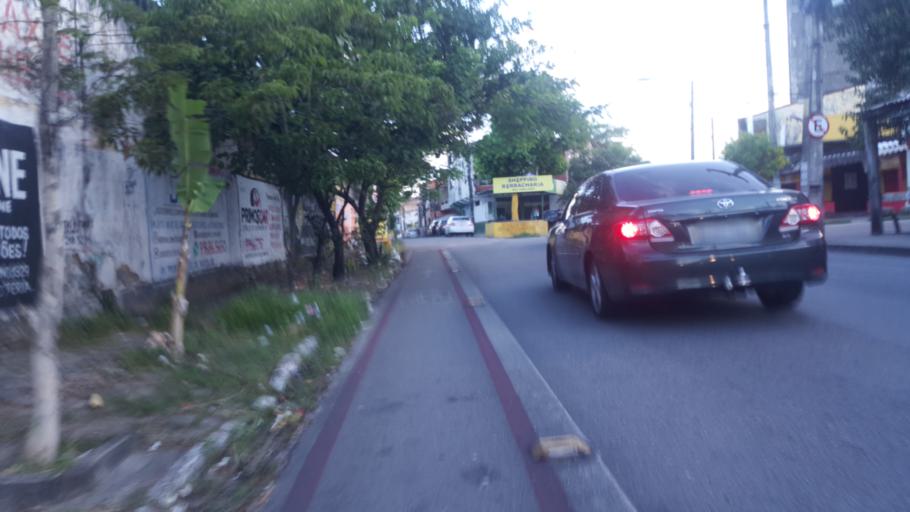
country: BR
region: Ceara
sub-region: Fortaleza
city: Fortaleza
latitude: -3.7536
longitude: -38.5403
